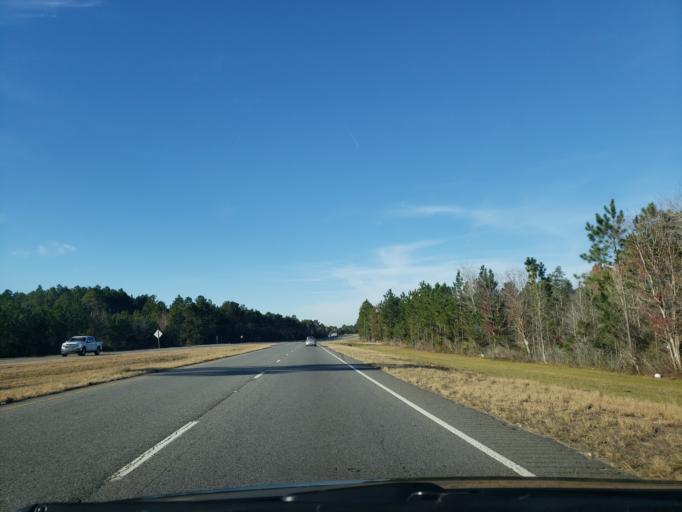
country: US
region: Georgia
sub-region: Ware County
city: Deenwood
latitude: 31.2265
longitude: -82.4256
